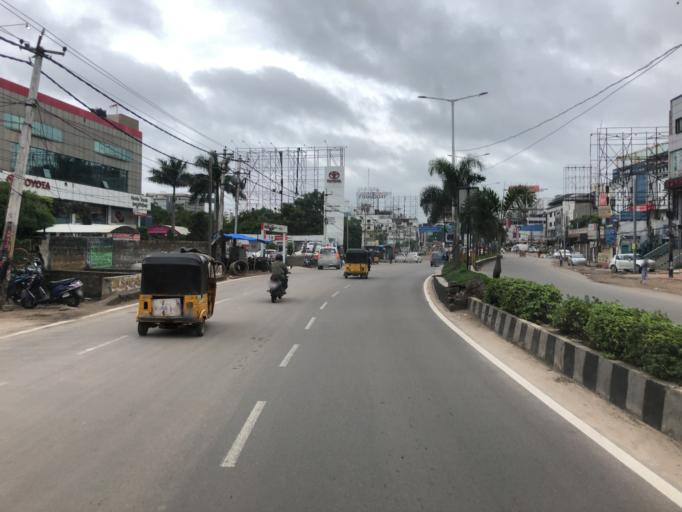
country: IN
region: Telangana
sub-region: Rangareddi
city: Kukatpalli
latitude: 17.4617
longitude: 78.3672
